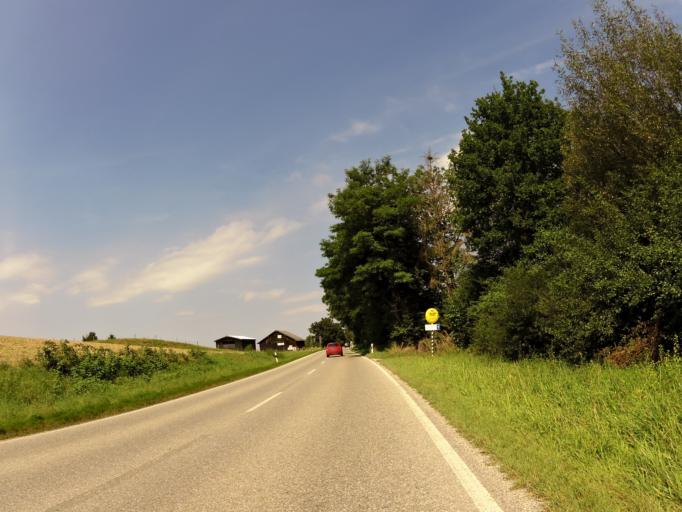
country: DE
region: Bavaria
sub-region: Upper Bavaria
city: Herrsching am Ammersee
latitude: 48.0247
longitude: 11.1429
